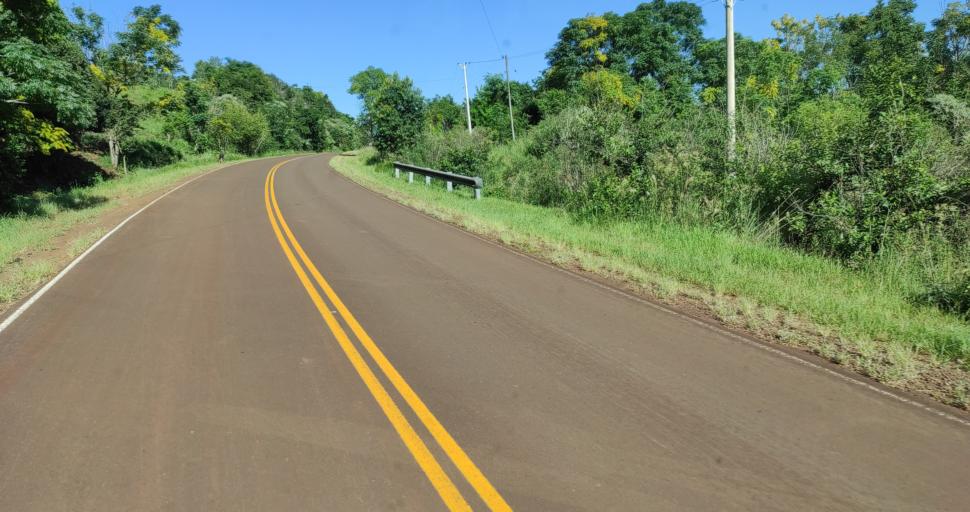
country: AR
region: Misiones
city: El Soberbio
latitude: -27.2256
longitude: -54.0603
